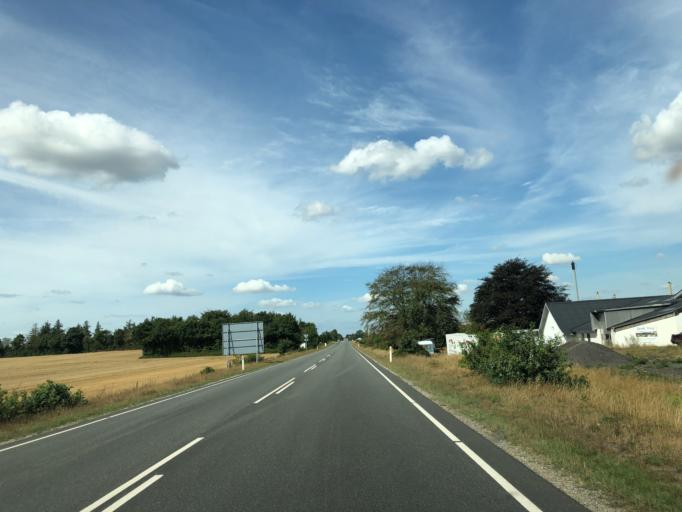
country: DK
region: Central Jutland
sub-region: Ikast-Brande Kommune
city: Bording Kirkeby
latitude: 56.1409
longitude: 9.2711
